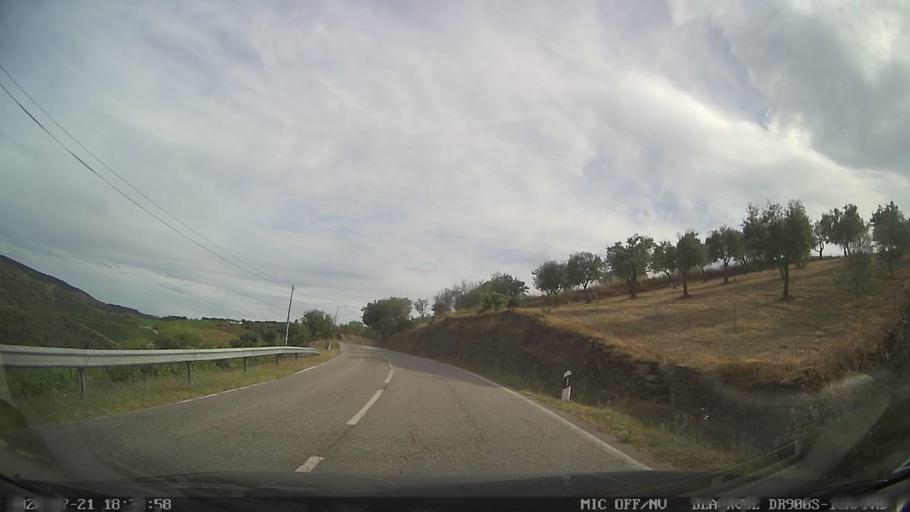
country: PT
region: Viseu
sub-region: Sao Joao da Pesqueira
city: Sao Joao da Pesqueira
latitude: 41.0797
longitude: -7.3889
